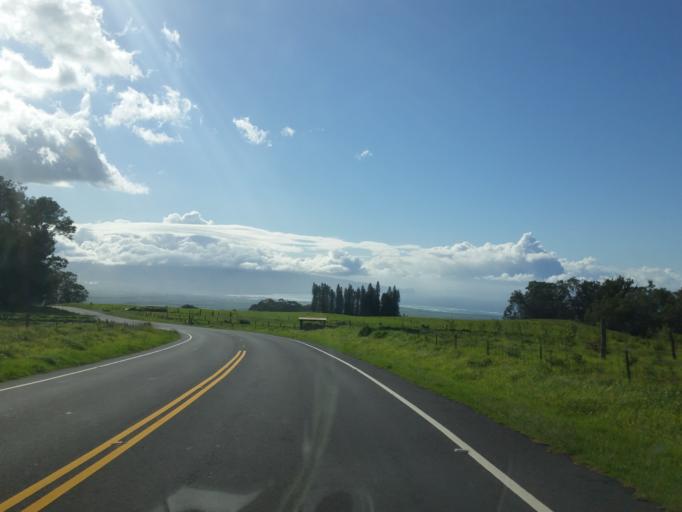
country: US
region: Hawaii
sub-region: Maui County
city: Pukalani
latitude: 20.8207
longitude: -156.3083
